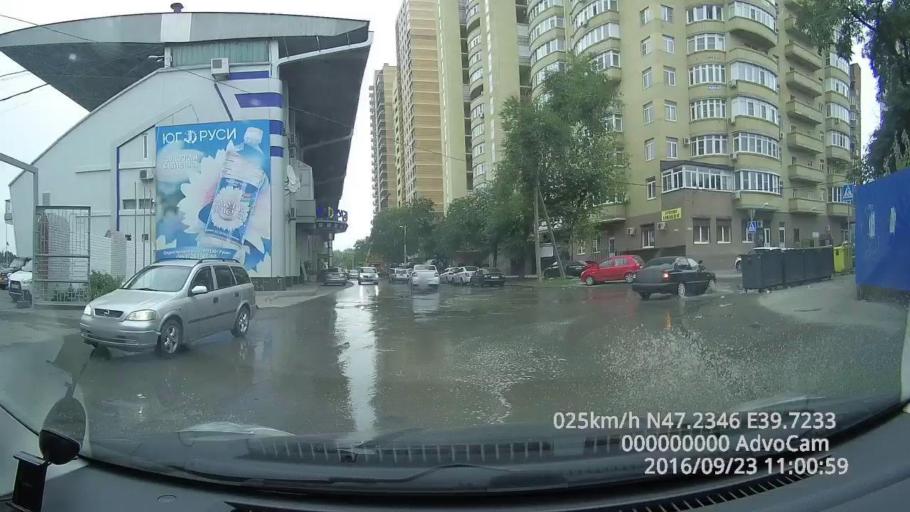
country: RU
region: Rostov
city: Rostov-na-Donu
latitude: 47.2346
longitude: 39.7235
